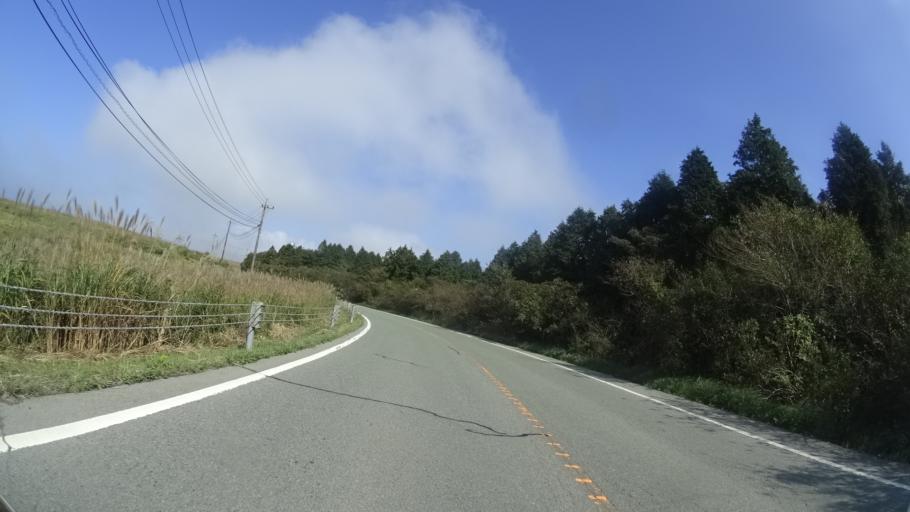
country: JP
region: Kumamoto
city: Aso
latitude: 32.9385
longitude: 130.9731
